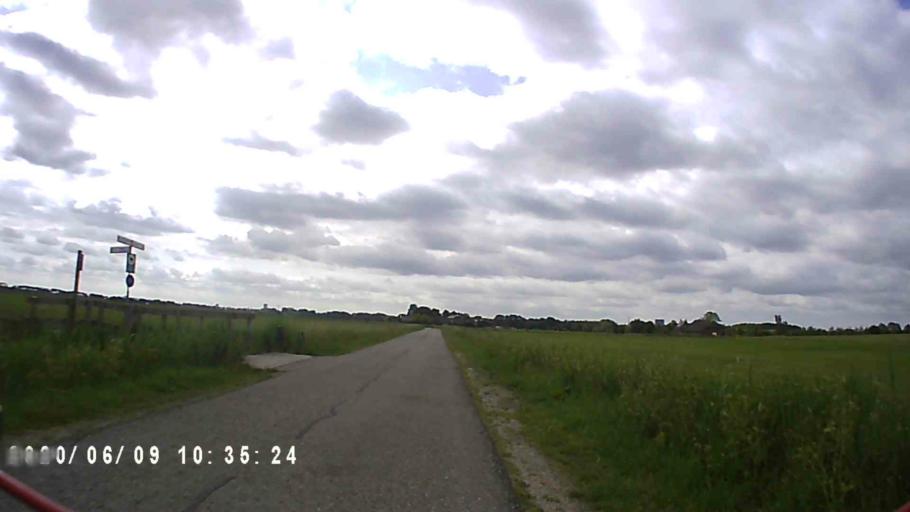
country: NL
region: Groningen
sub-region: Gemeente Groningen
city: Korrewegwijk
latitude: 53.2603
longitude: 6.5234
